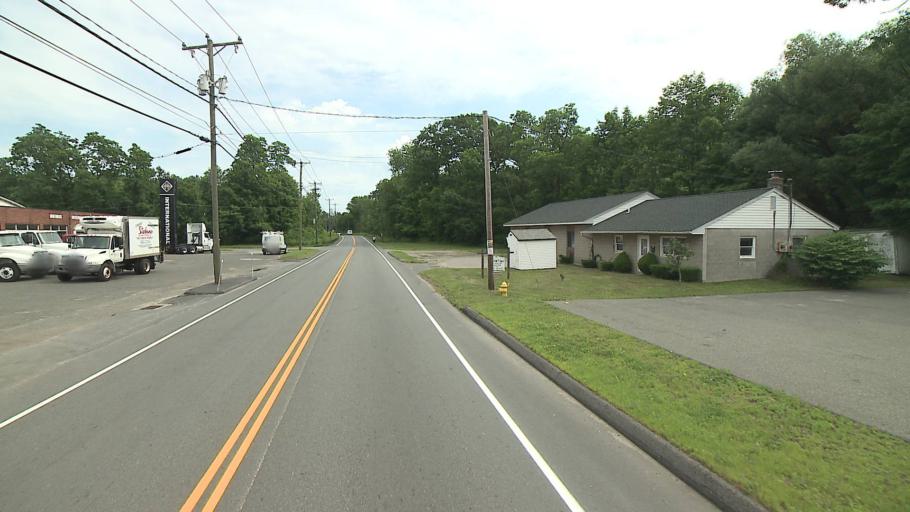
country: US
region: Connecticut
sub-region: Litchfield County
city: Torrington
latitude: 41.7790
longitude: -73.1185
